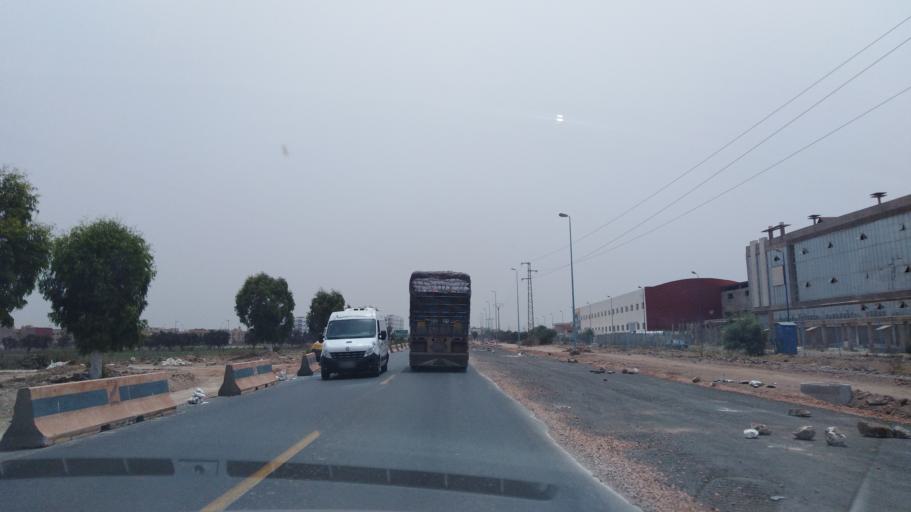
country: MA
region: Grand Casablanca
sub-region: Mediouna
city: Mediouna
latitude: 33.3933
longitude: -7.5353
